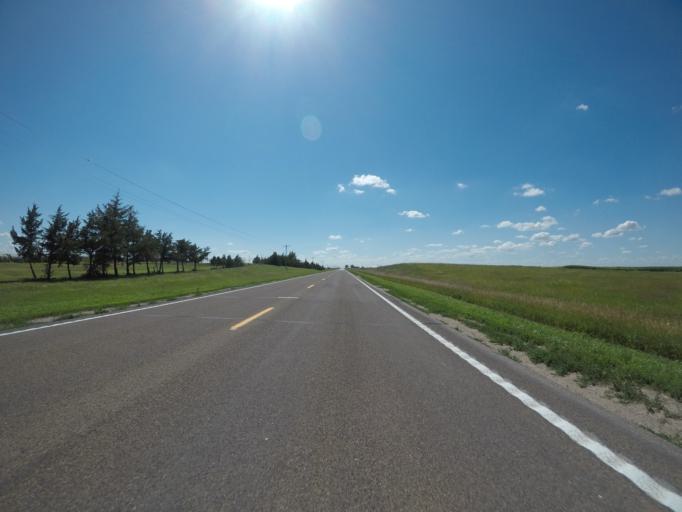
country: US
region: Nebraska
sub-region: Chase County
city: Imperial
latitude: 40.5376
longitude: -101.8385
